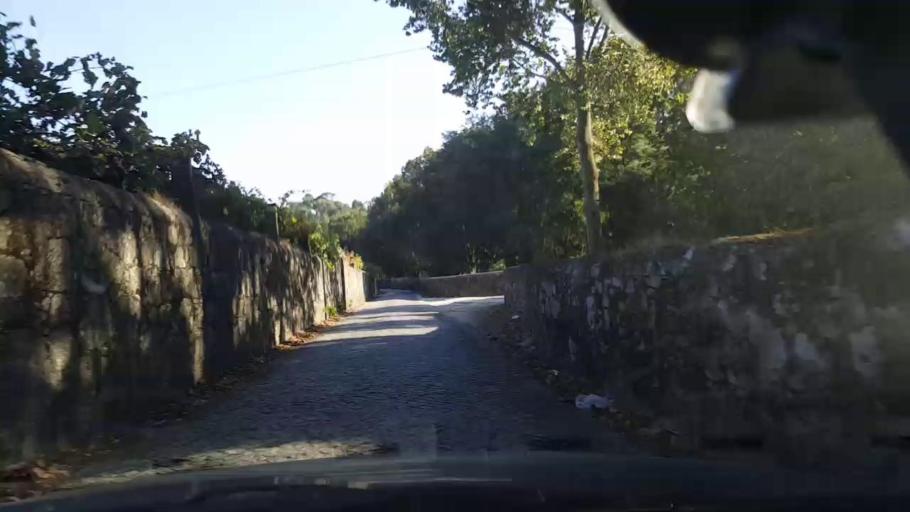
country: PT
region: Porto
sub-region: Vila do Conde
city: Arvore
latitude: 41.3424
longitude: -8.6870
